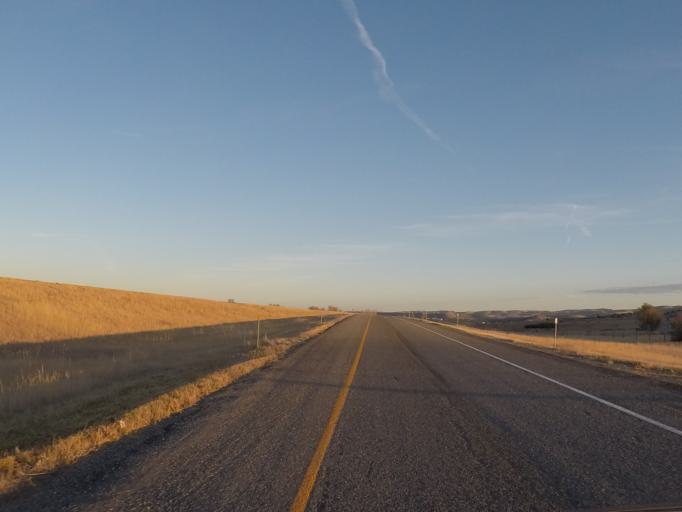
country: US
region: Montana
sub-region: Sweet Grass County
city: Big Timber
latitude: 45.7682
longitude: -109.7939
